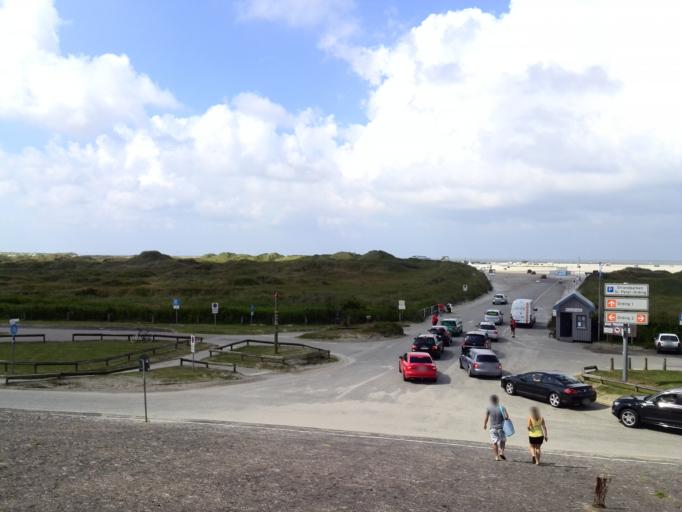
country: DE
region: Schleswig-Holstein
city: Sankt Peter-Ording
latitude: 54.3341
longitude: 8.6044
